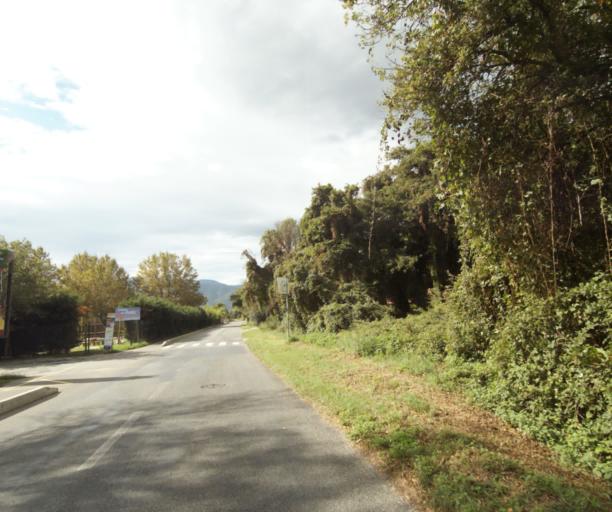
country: FR
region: Languedoc-Roussillon
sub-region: Departement des Pyrenees-Orientales
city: Argelers
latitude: 42.5585
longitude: 3.0300
